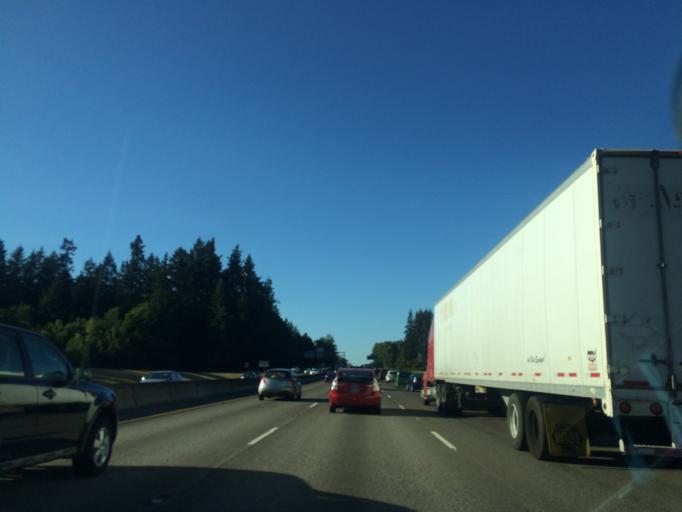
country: US
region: Oregon
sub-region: Clackamas County
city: Wilsonville
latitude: 45.2854
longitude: -122.7693
